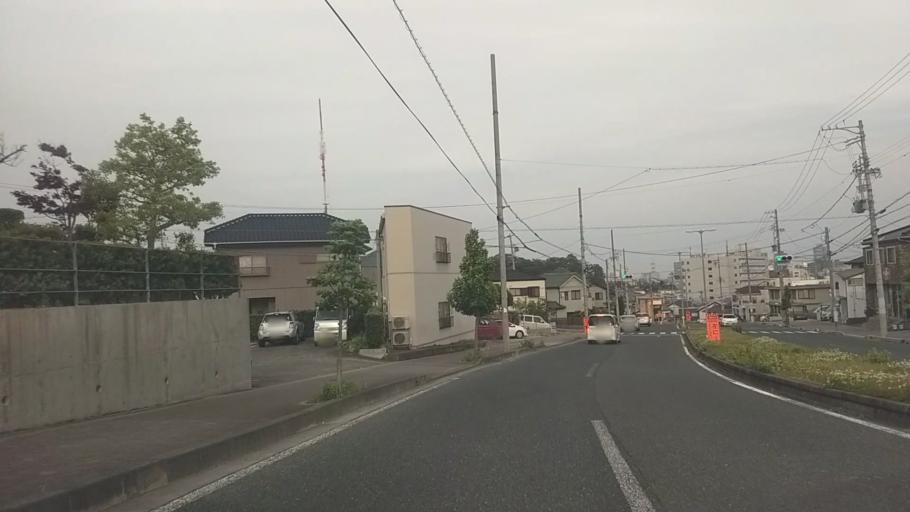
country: JP
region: Shizuoka
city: Hamamatsu
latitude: 34.7192
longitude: 137.7199
